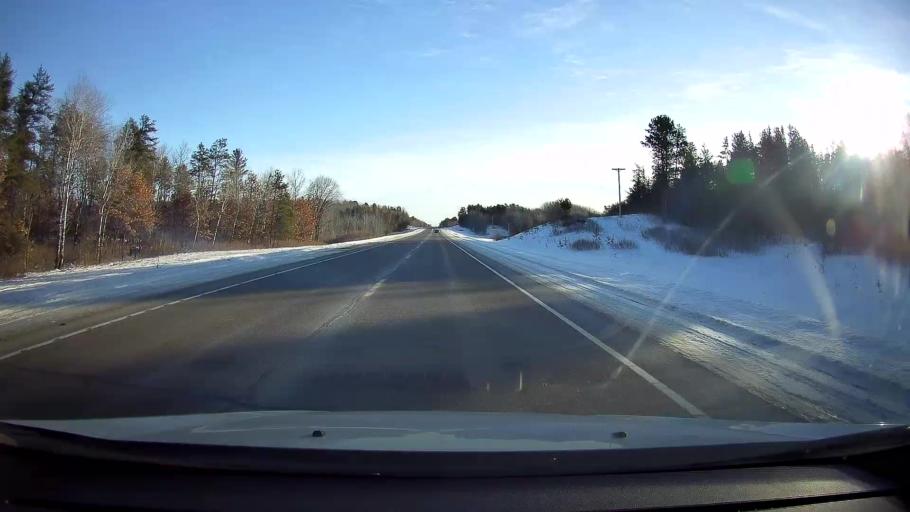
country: US
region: Wisconsin
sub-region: Washburn County
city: Spooner
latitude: 45.9104
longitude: -91.7930
